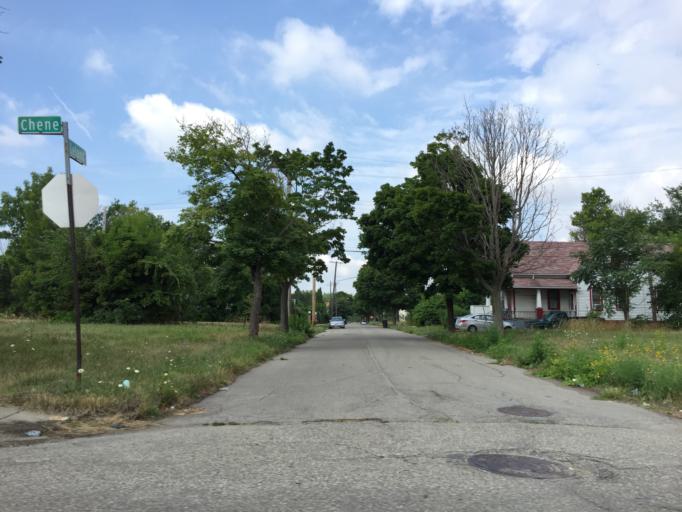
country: US
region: Michigan
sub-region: Wayne County
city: Detroit
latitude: 42.3585
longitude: -83.0361
